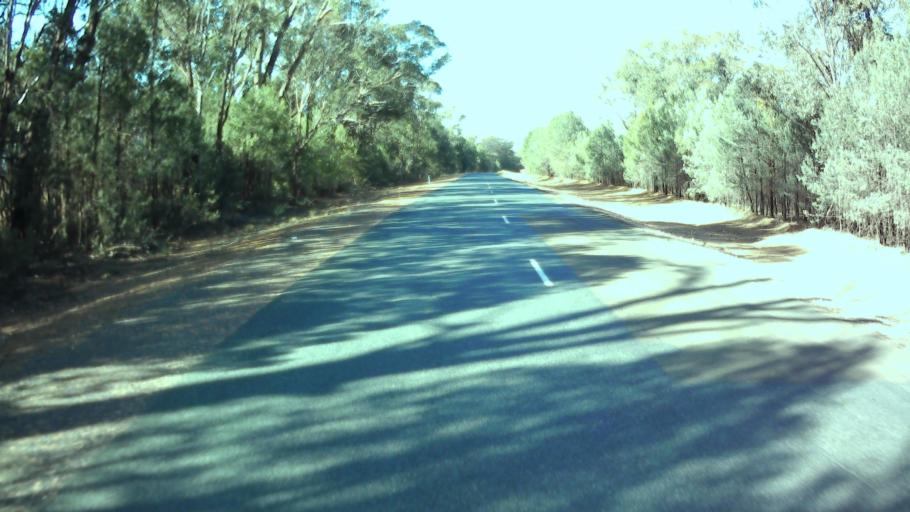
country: AU
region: New South Wales
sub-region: Weddin
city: Grenfell
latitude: -34.0309
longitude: 148.0931
